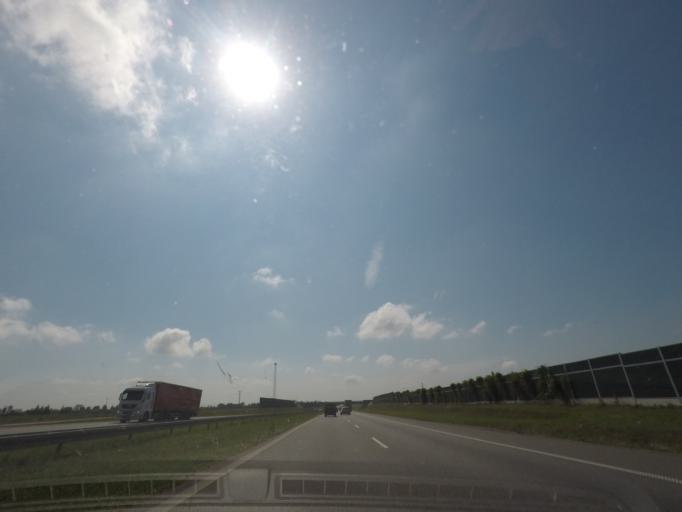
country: PL
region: Kujawsko-Pomorskie
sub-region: Powiat wloclawski
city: Czerniewice
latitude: 52.5161
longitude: 19.1083
